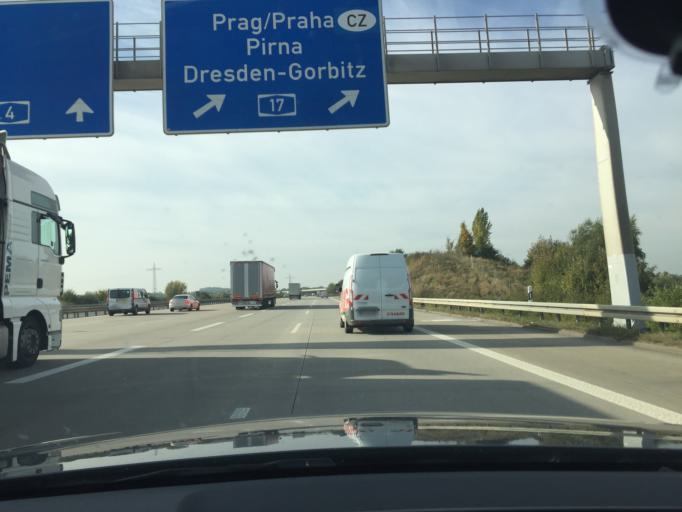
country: DE
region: Saxony
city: Radebeul
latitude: 51.0652
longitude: 13.6150
